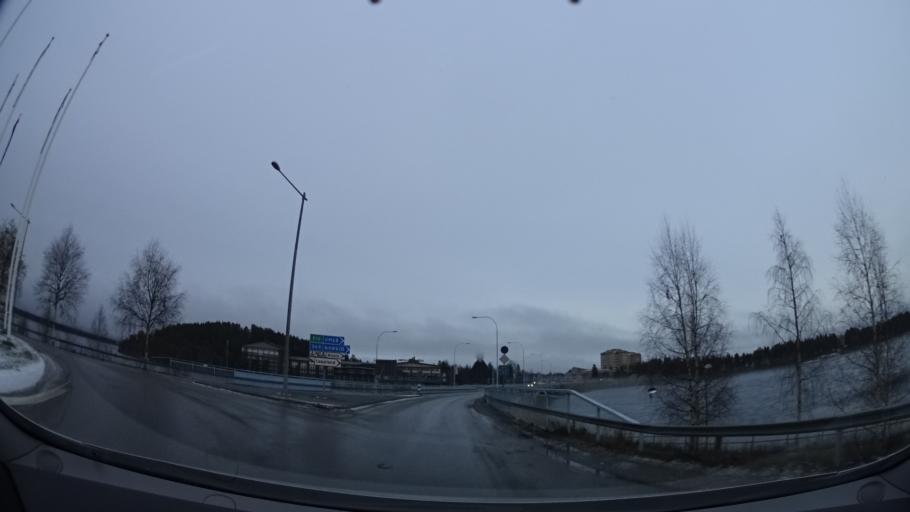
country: SE
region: Vaesterbotten
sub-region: Lycksele Kommun
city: Lycksele
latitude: 64.5898
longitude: 18.6840
